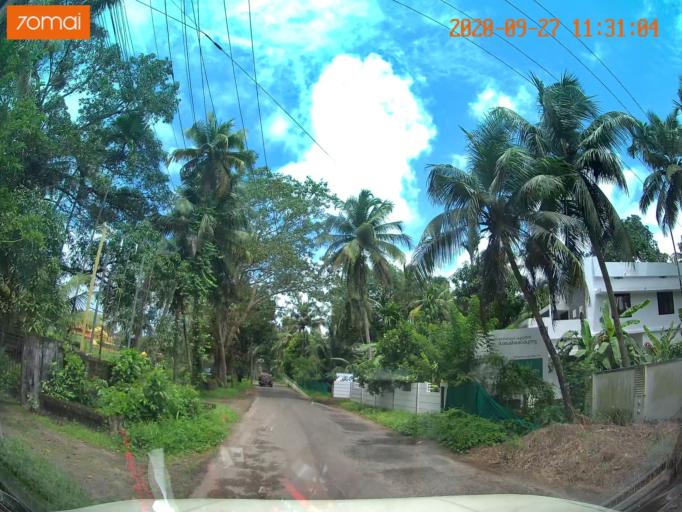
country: IN
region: Kerala
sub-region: Thrissur District
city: Thanniyam
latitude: 10.4212
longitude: 76.1335
